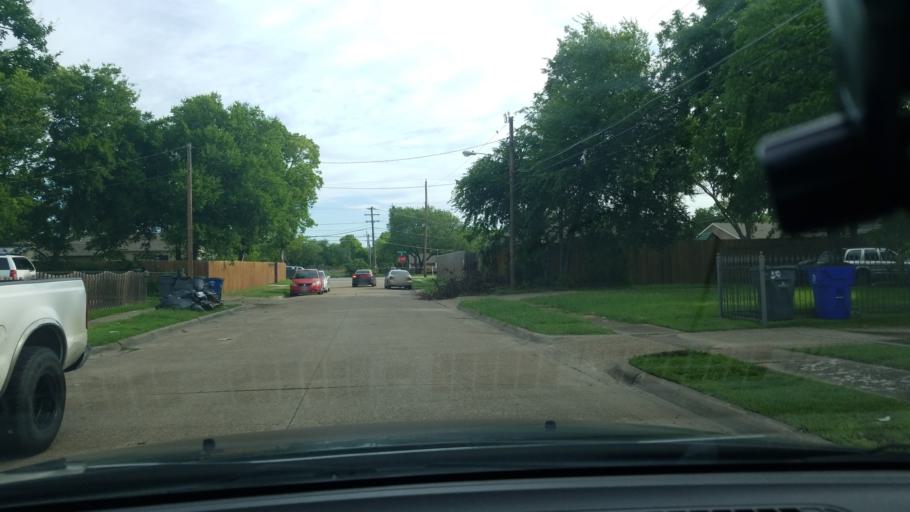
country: US
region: Texas
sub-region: Dallas County
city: Balch Springs
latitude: 32.7625
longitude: -96.6640
